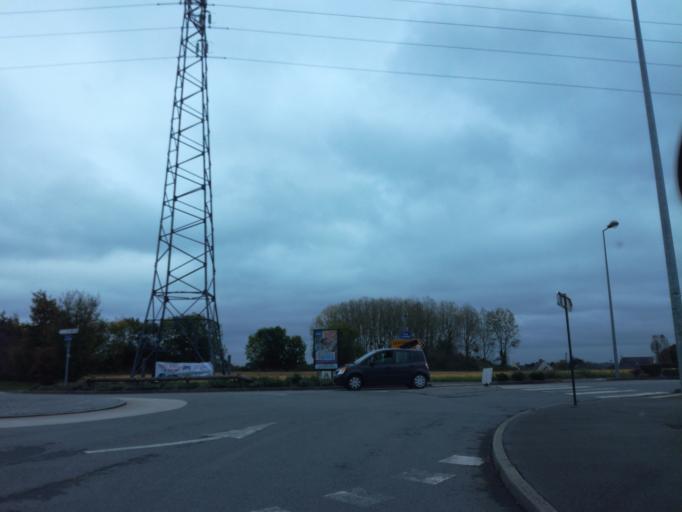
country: FR
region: Brittany
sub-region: Departement d'Ille-et-Vilaine
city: La Richardais
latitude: 48.6122
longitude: -2.0461
